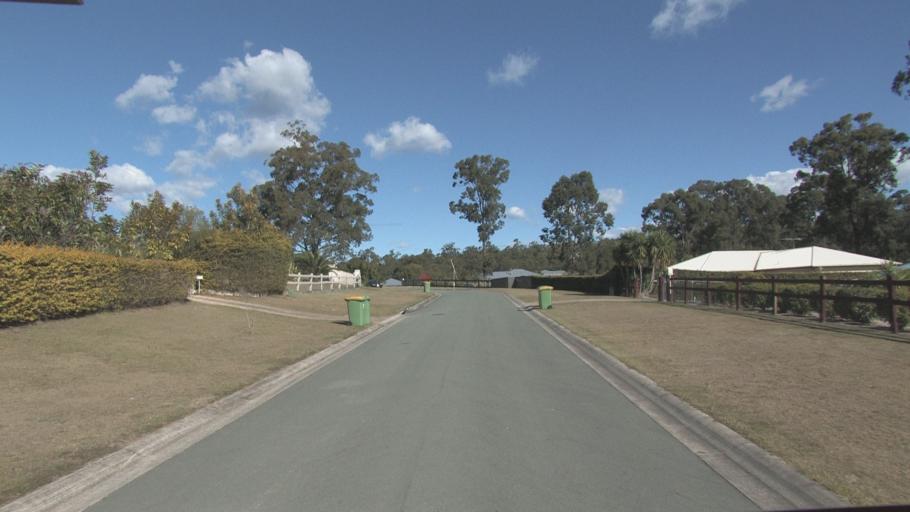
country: AU
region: Queensland
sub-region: Ipswich
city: Springfield Lakes
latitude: -27.7324
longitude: 152.9090
